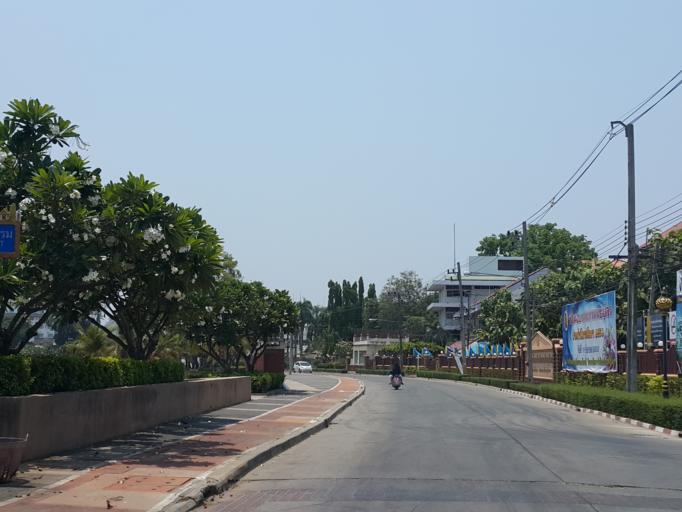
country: TH
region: Phitsanulok
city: Phitsanulok
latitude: 16.8210
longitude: 100.2580
